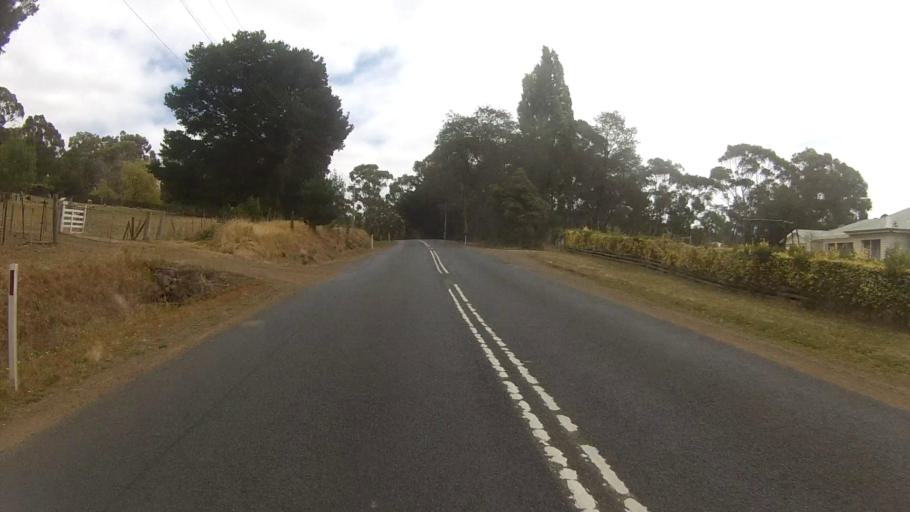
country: AU
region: Tasmania
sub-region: Kingborough
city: Margate
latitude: -43.0201
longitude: 147.2537
